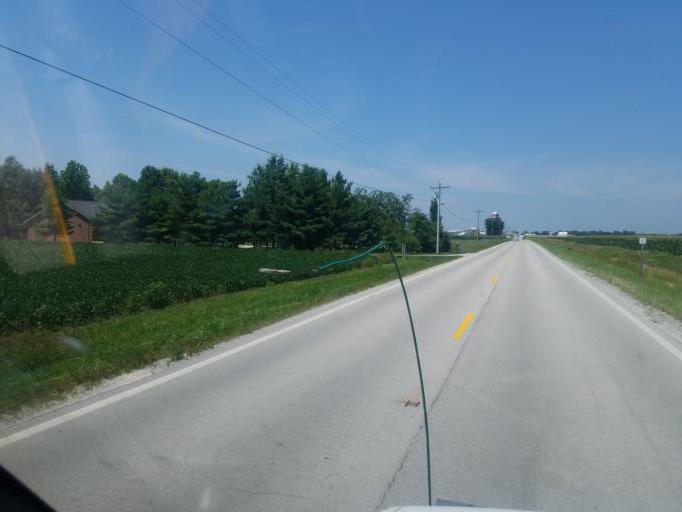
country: US
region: Ohio
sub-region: Shelby County
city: Fort Loramie
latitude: 40.3684
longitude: -84.4341
